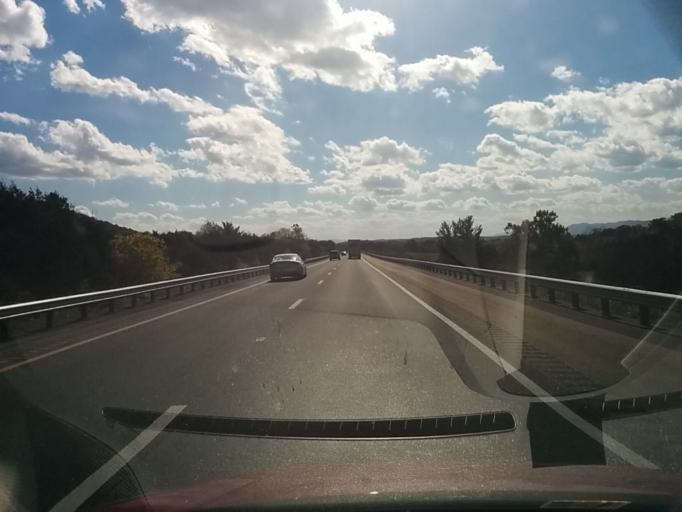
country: US
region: Virginia
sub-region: Rockbridge County
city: East Lexington
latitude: 37.8160
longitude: -79.3836
